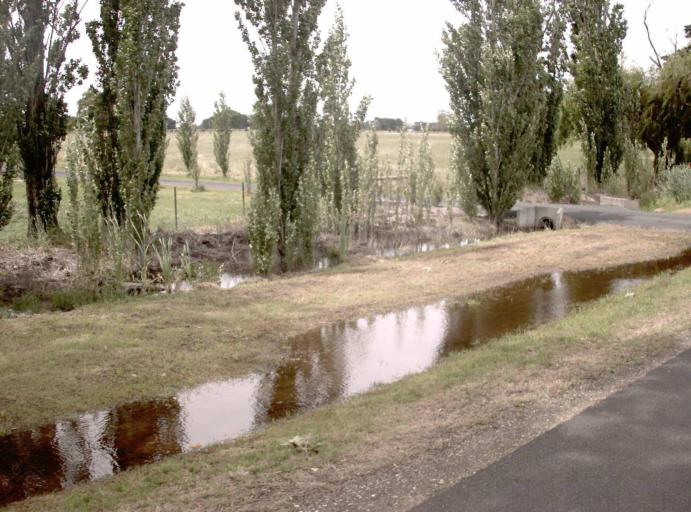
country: AU
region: Victoria
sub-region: Wellington
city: Sale
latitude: -38.0527
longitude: 147.0241
